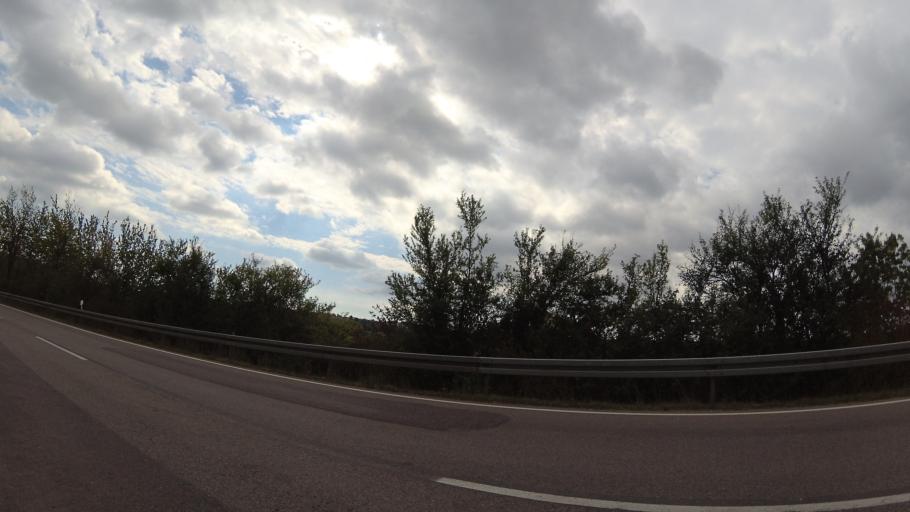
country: FR
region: Lorraine
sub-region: Departement de la Moselle
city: Sarreinsming
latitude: 49.1413
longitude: 7.1131
